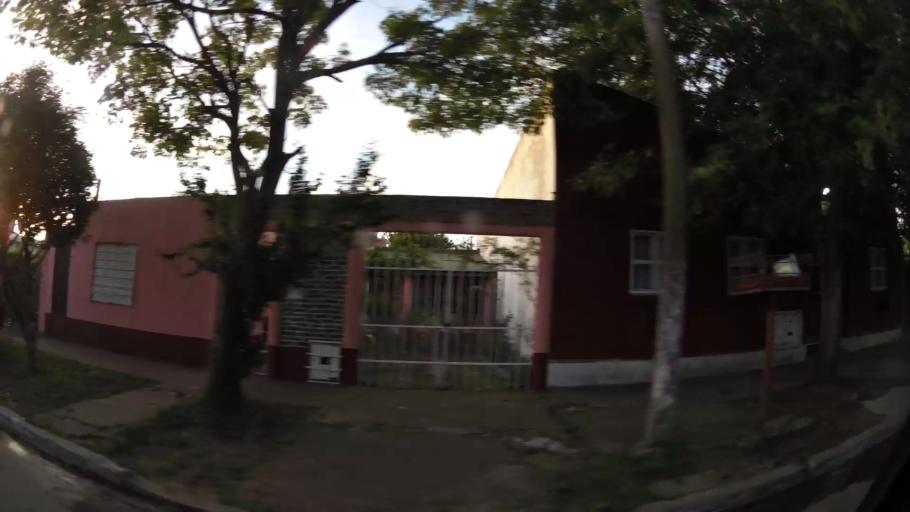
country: AR
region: Buenos Aires
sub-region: Partido de Quilmes
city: Quilmes
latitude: -34.7890
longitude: -58.2214
